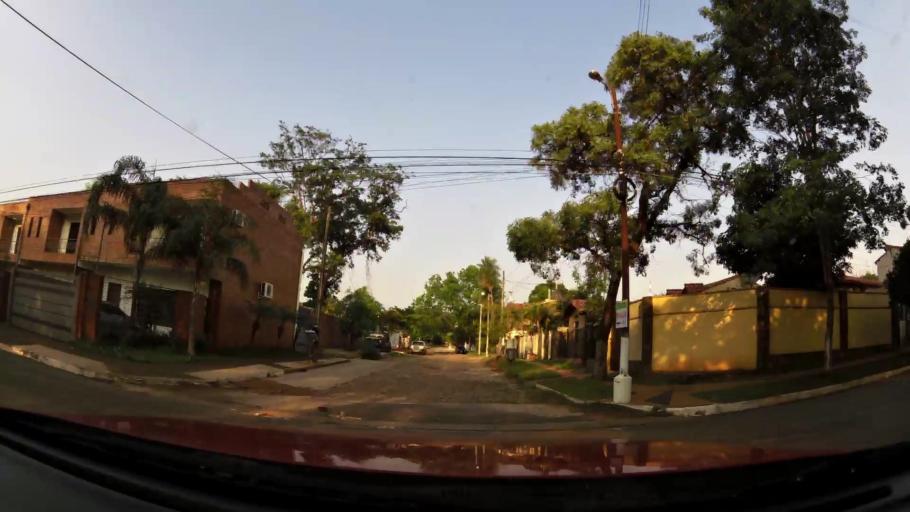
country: PY
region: Central
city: Lambare
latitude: -25.3481
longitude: -57.6045
